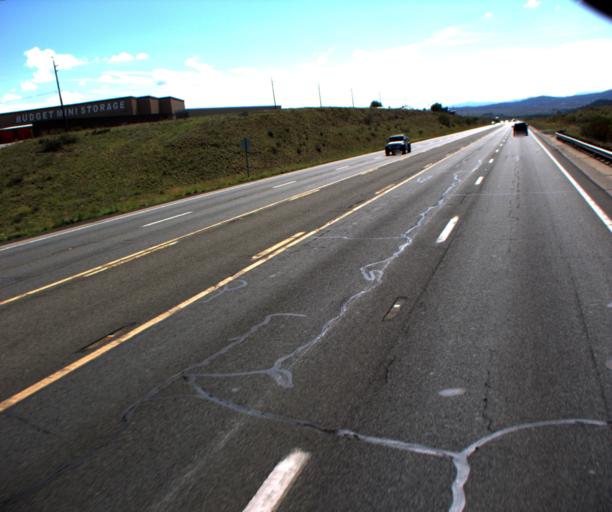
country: US
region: Arizona
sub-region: Yavapai County
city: Prescott Valley
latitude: 34.5825
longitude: -112.3072
